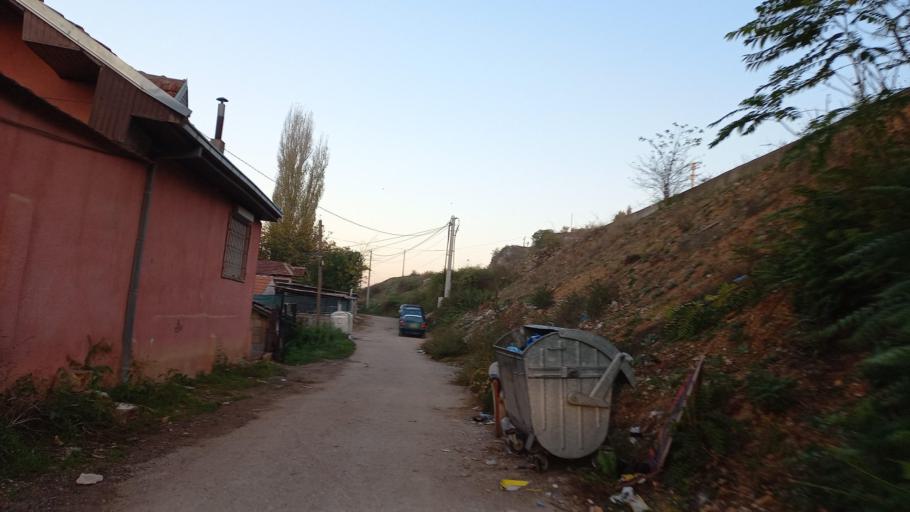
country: MK
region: Kumanovo
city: Kumanovo
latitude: 42.1392
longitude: 21.7274
